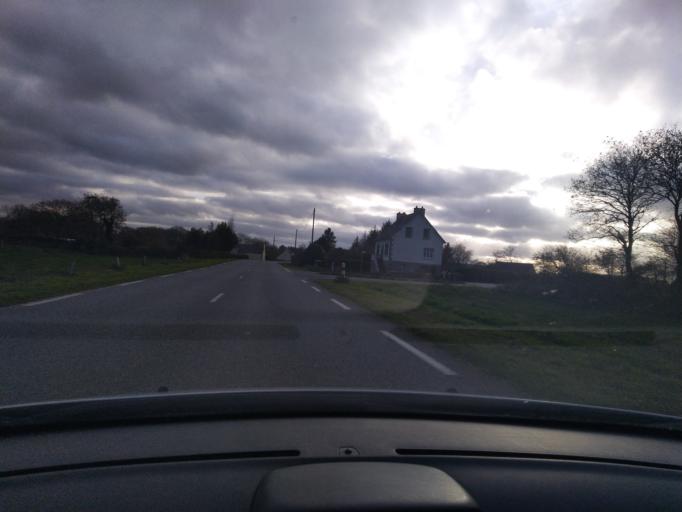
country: FR
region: Brittany
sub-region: Departement des Cotes-d'Armor
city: Plouaret
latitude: 48.5982
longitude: -3.4916
